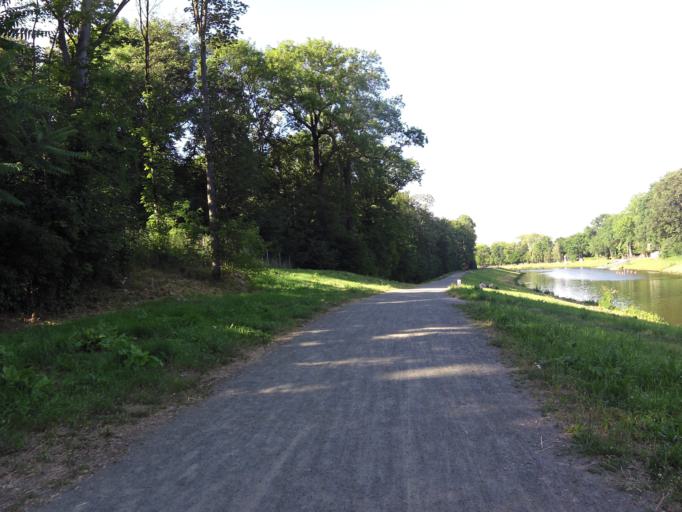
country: DE
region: Saxony
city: Leipzig
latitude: 51.3199
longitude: 12.3536
